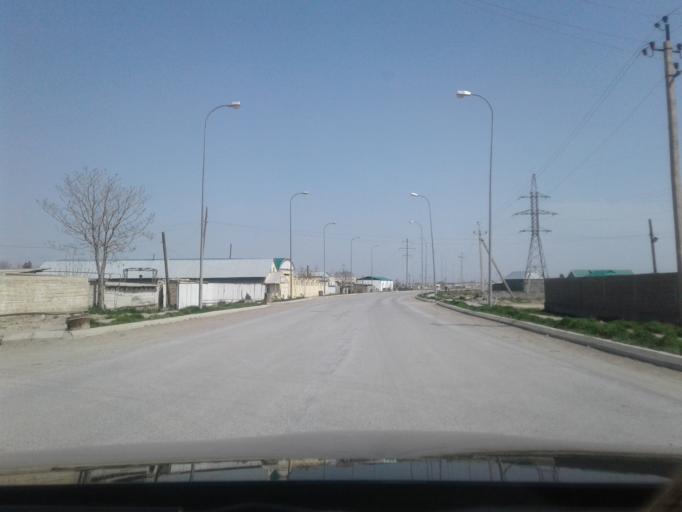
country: TM
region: Ahal
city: Abadan
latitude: 38.1600
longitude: 57.9779
